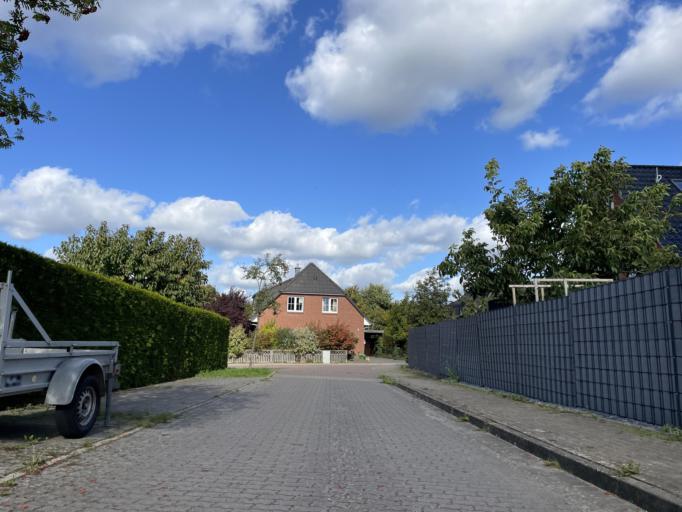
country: DE
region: Lower Saxony
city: Barendorf
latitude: 53.2339
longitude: 10.5214
